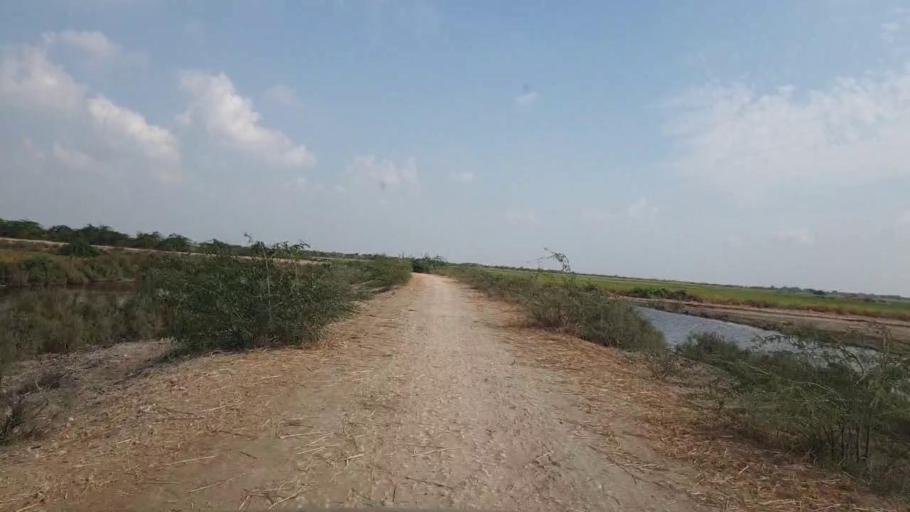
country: PK
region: Sindh
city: Badin
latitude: 24.4748
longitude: 68.5952
